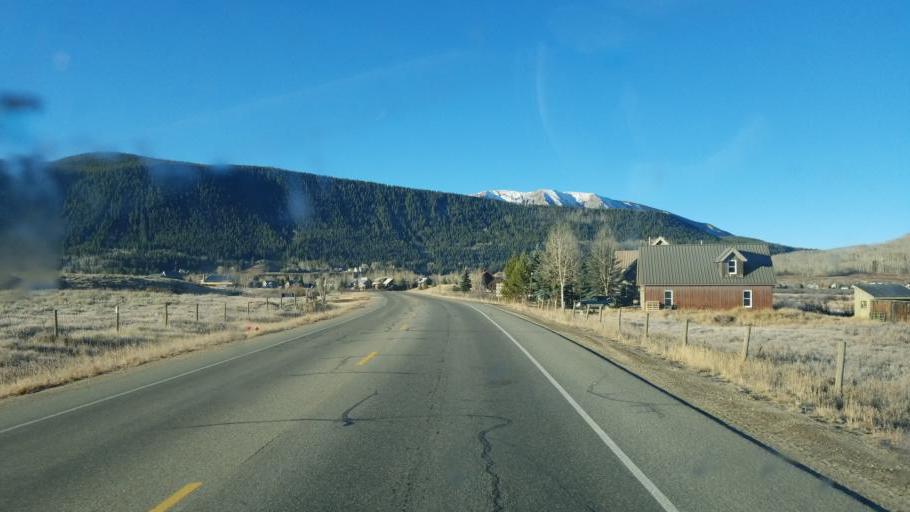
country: US
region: Colorado
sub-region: Gunnison County
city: Crested Butte
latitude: 38.8762
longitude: -106.9786
